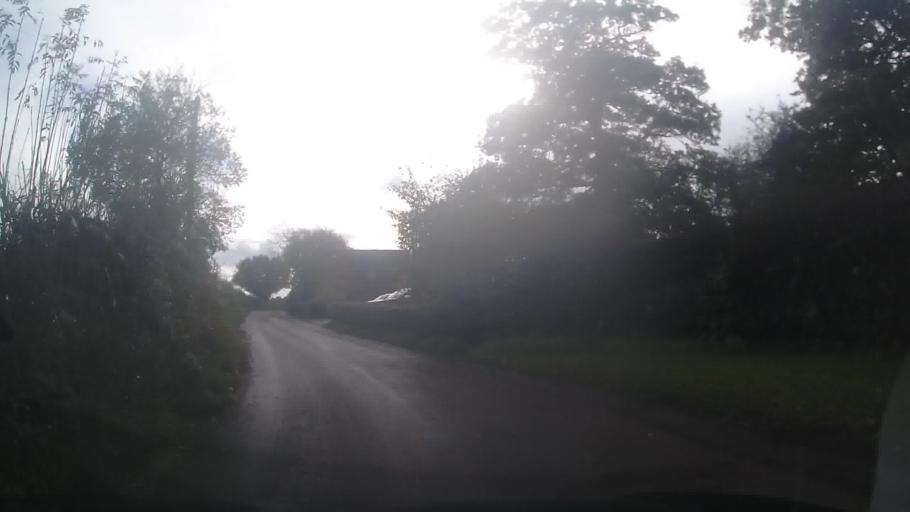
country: GB
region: England
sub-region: Shropshire
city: Whitchurch
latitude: 52.9469
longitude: -2.7008
